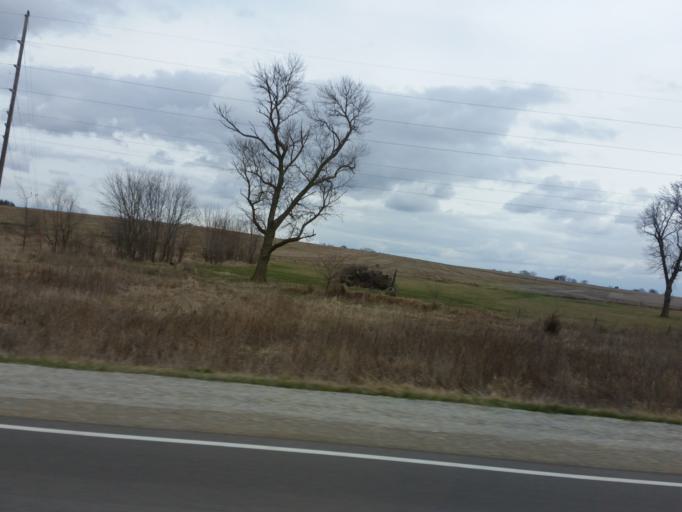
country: US
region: Iowa
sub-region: Black Hawk County
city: Elk Run Heights
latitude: 42.4896
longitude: -92.2194
